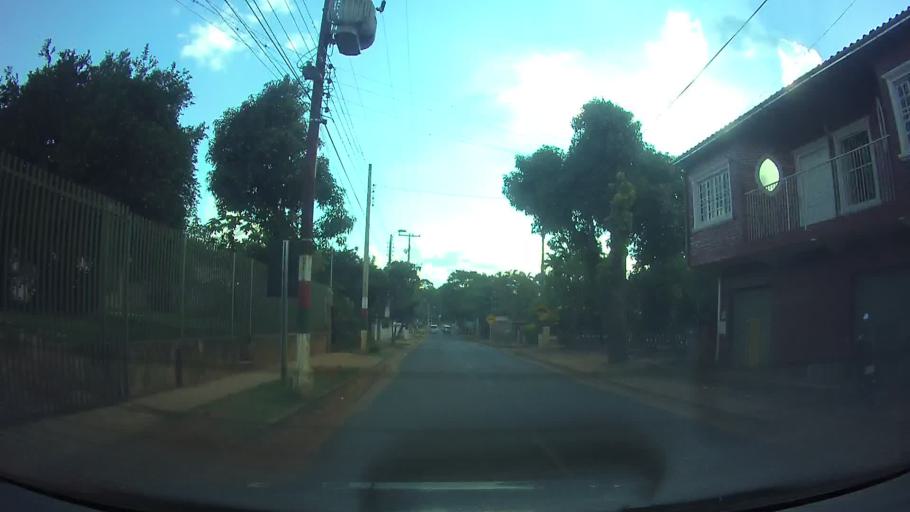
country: PY
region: Central
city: Aregua
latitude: -25.2811
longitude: -57.4341
